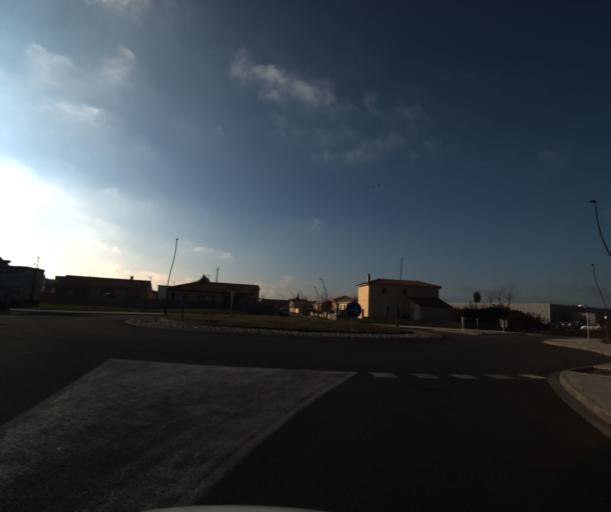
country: FR
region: Midi-Pyrenees
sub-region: Departement de la Haute-Garonne
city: Colomiers
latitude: 43.5964
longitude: 1.3589
